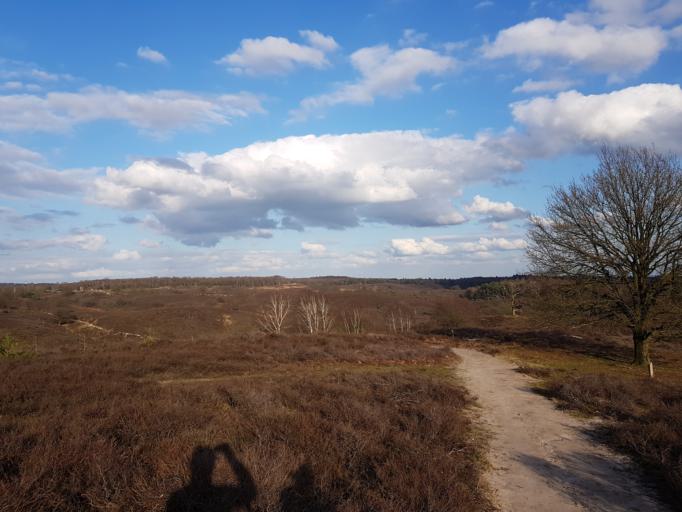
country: NL
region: Gelderland
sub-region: Gemeente Rheden
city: Rheden
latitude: 52.0236
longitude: 6.0107
